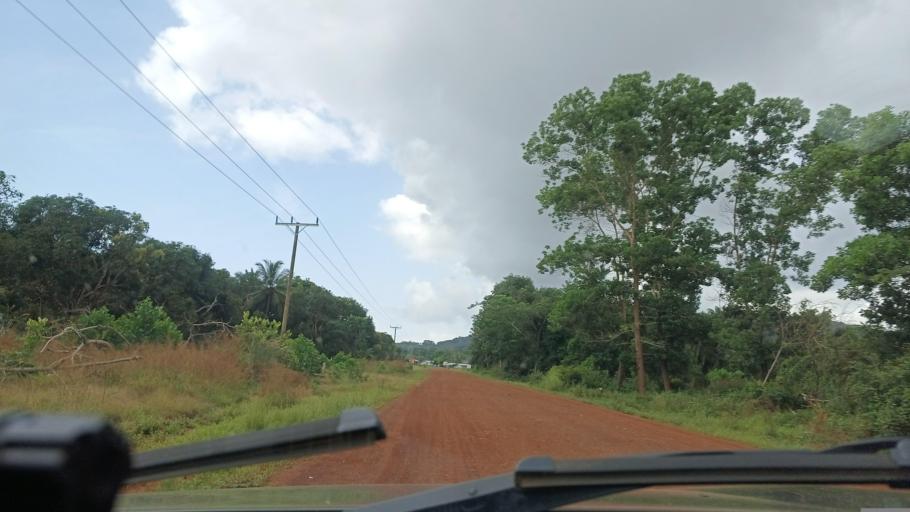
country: LR
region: Grand Cape Mount
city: Robertsport
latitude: 6.7051
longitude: -11.3298
